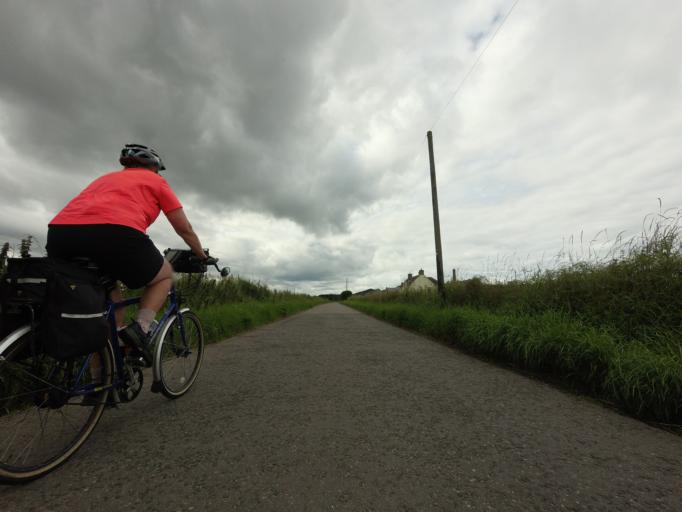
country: GB
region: Scotland
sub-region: Moray
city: Forres
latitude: 57.6258
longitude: -3.6524
